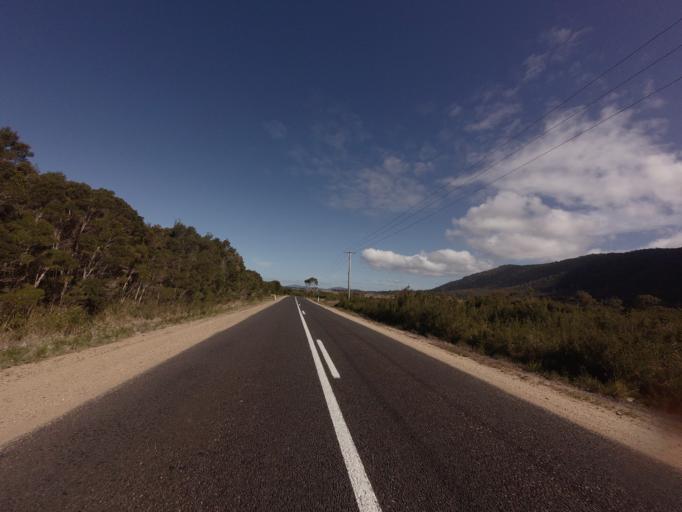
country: AU
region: Tasmania
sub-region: Break O'Day
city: St Helens
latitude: -41.7151
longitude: 148.2747
